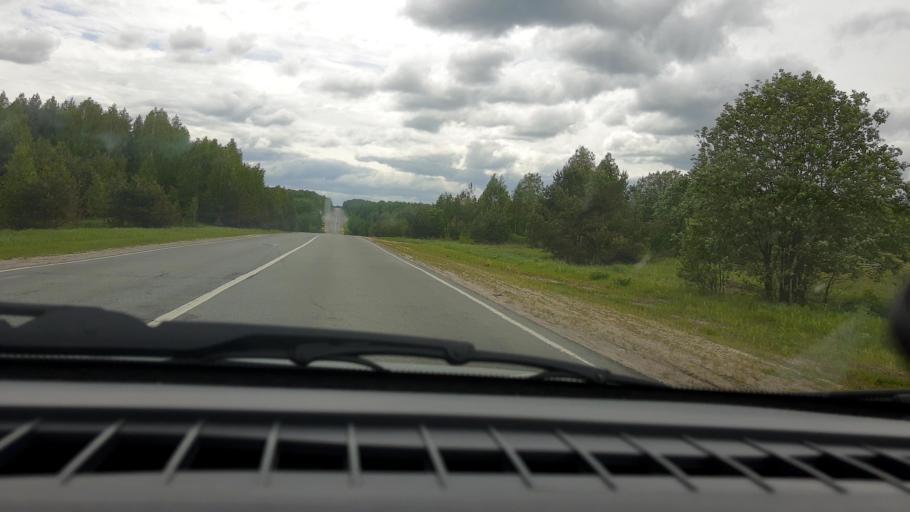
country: RU
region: Nizjnij Novgorod
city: Krasnyye Baki
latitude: 56.9798
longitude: 45.1156
